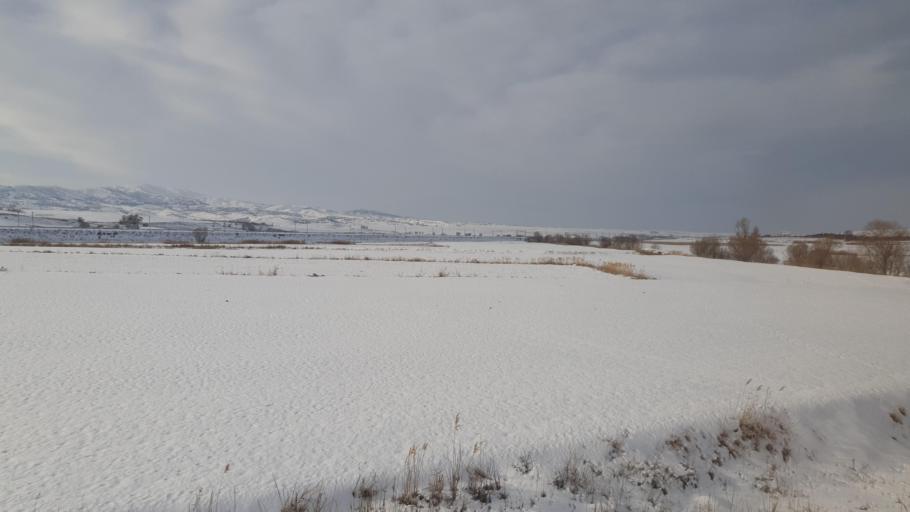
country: TR
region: Kirikkale
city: Baliseyh
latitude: 39.9278
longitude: 33.7810
